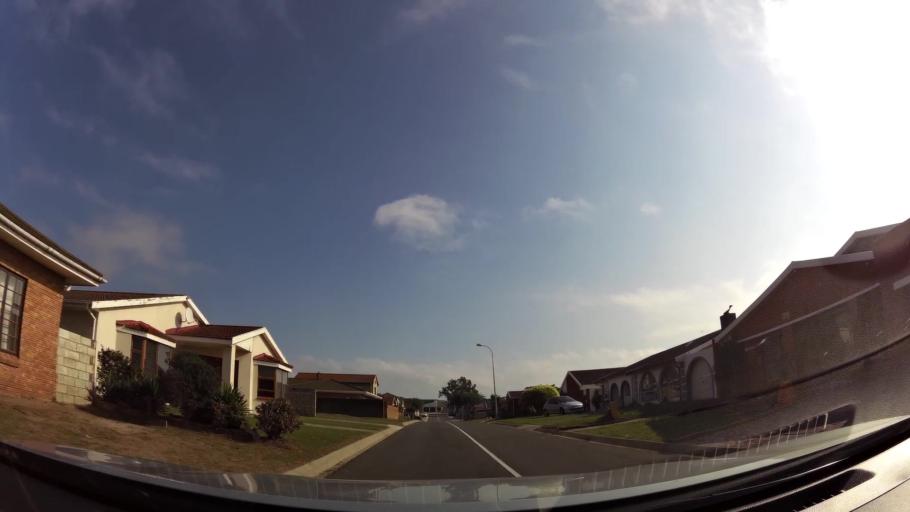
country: ZA
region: Eastern Cape
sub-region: Nelson Mandela Bay Metropolitan Municipality
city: Port Elizabeth
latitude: -33.9235
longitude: 25.5318
